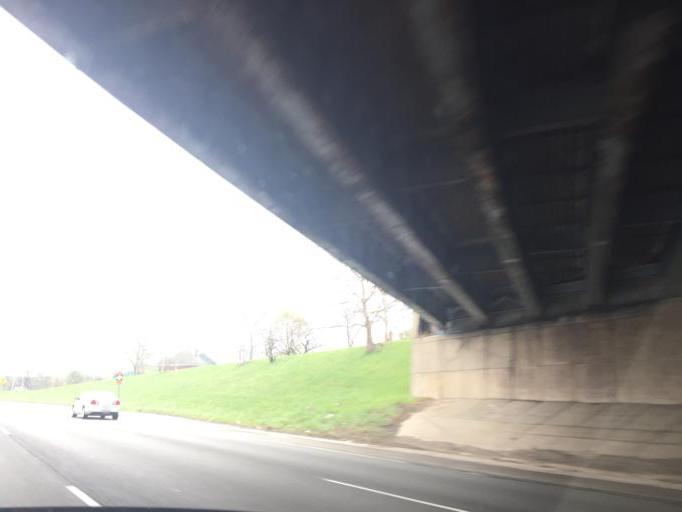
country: US
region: Michigan
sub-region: Wayne County
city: Highland Park
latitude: 42.3557
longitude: -83.1104
